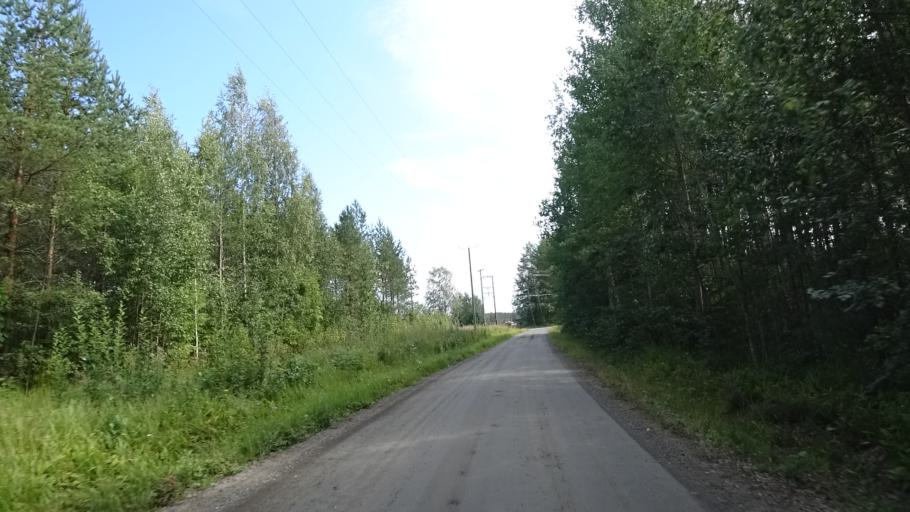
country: FI
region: North Karelia
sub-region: Joensuu
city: Pyhaeselkae
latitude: 62.3725
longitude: 29.8358
